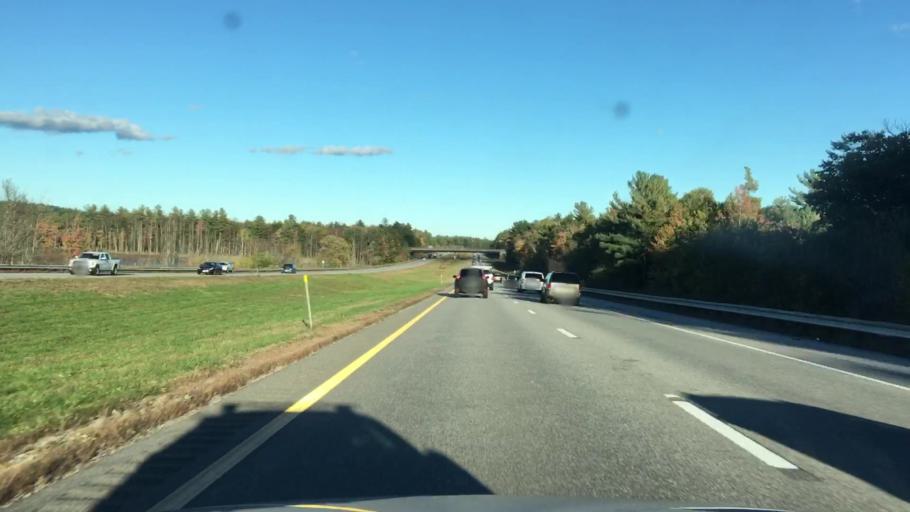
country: US
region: New Hampshire
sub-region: Rockingham County
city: Candia
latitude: 43.0404
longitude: -71.2887
